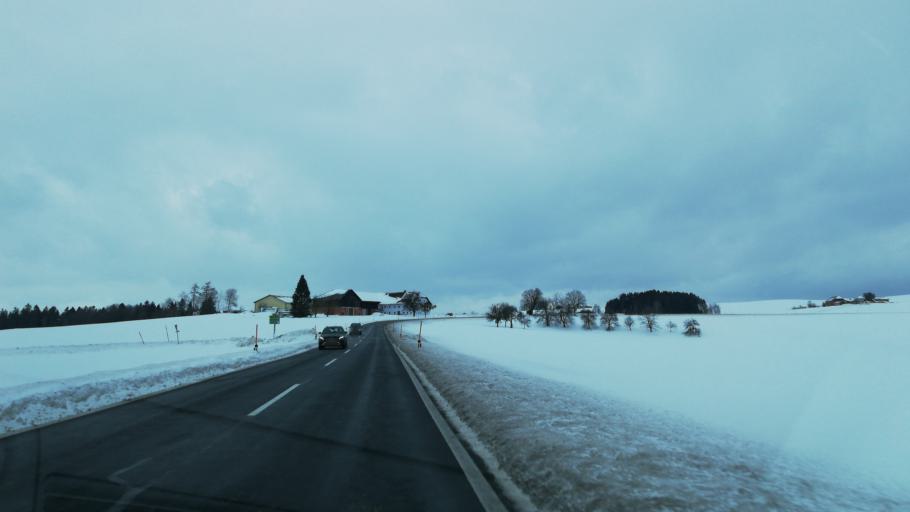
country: AT
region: Upper Austria
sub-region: Politischer Bezirk Urfahr-Umgebung
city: Herzogsdorf
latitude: 48.4628
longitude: 14.1211
